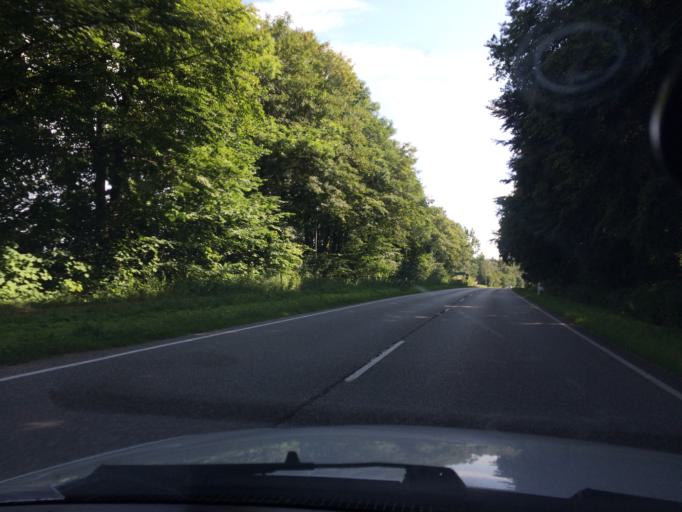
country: DE
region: Schleswig-Holstein
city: Sankelmark
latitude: 54.7195
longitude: 9.4440
